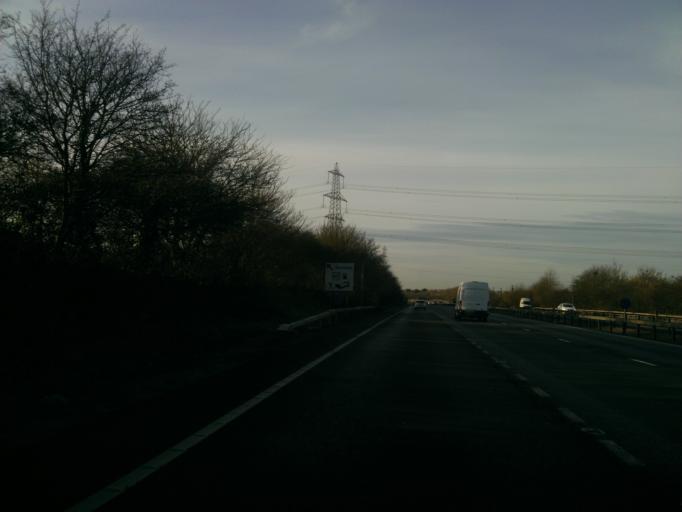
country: GB
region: England
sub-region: Essex
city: Hatfield Peverel
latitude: 51.7627
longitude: 0.5379
